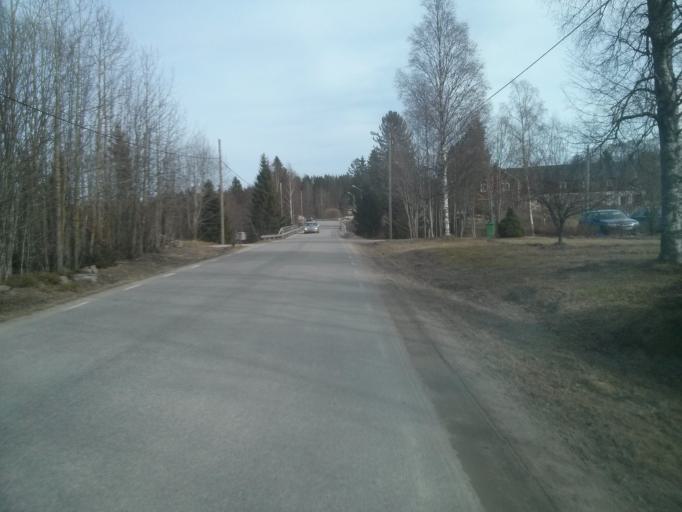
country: SE
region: Vaesternorrland
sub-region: Sundsvalls Kommun
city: Njurundabommen
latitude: 62.2366
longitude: 17.3886
